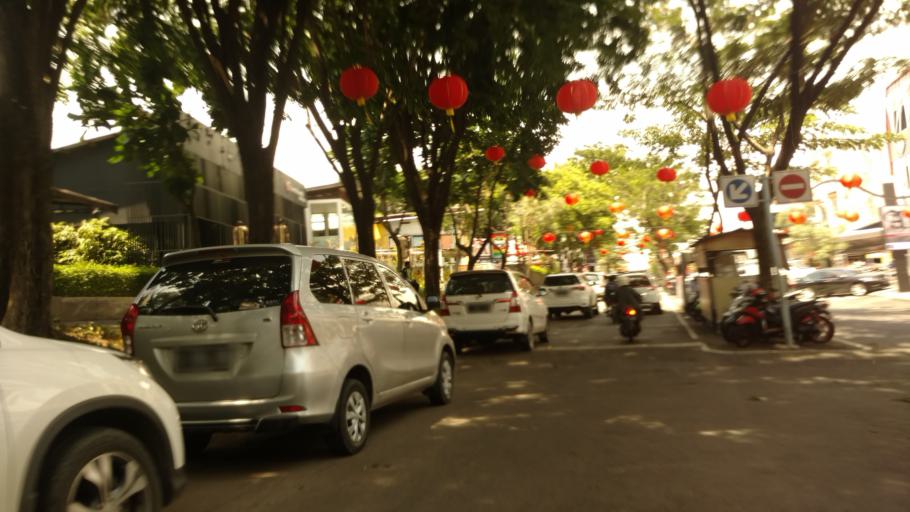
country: ID
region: East Java
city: Driyorejo
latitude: -7.2909
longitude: 112.6548
